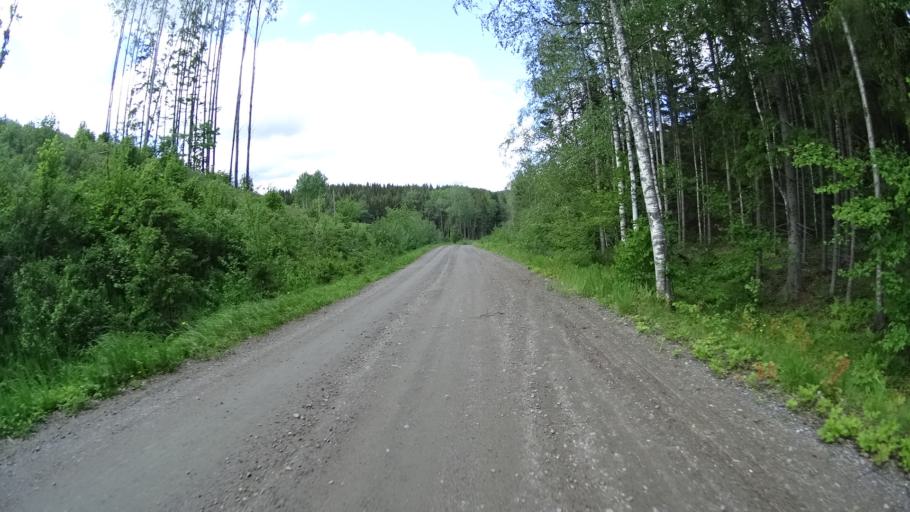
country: FI
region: Uusimaa
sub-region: Raaseporin
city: Pohja
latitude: 60.1612
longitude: 23.6060
